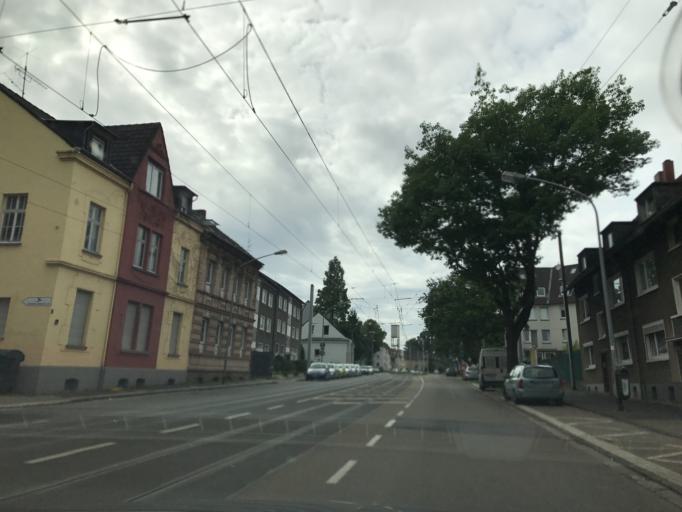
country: DE
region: North Rhine-Westphalia
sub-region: Regierungsbezirk Dusseldorf
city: Essen
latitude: 51.4761
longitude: 6.9620
